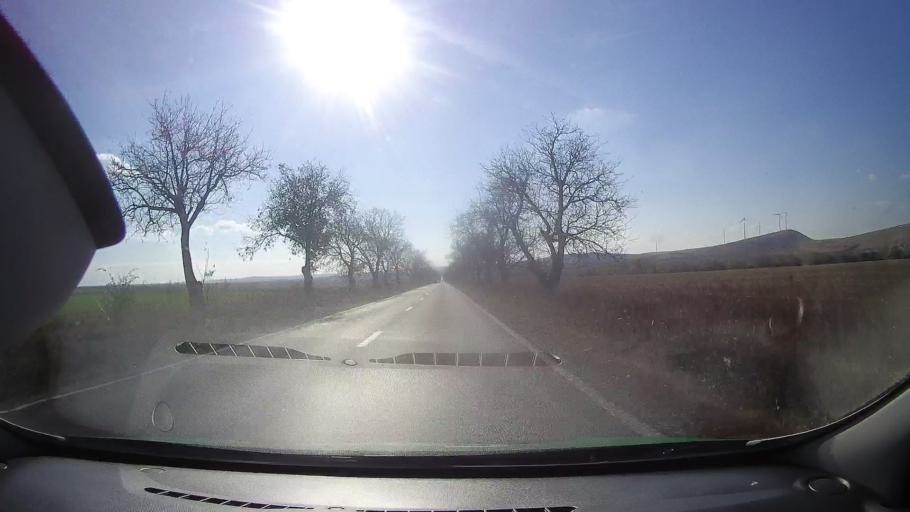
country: RO
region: Tulcea
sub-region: Comuna Ceamurlia de Jos
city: Ceamurlia de Jos
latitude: 44.7836
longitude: 28.6893
